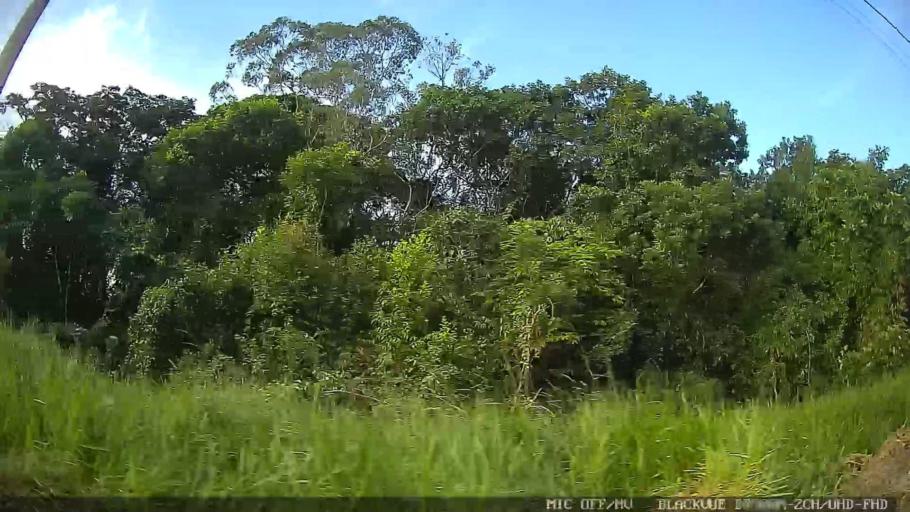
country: BR
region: Sao Paulo
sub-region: Itanhaem
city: Itanhaem
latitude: -24.1549
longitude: -46.7873
